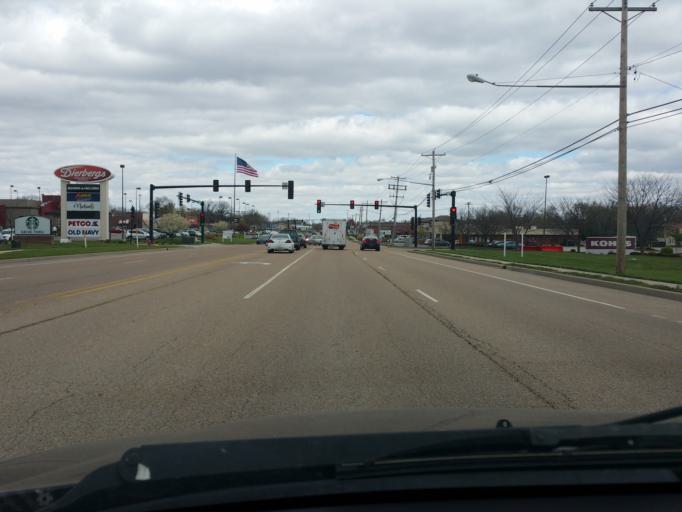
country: US
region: Illinois
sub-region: Madison County
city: Edwardsville
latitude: 38.7882
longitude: -89.9512
